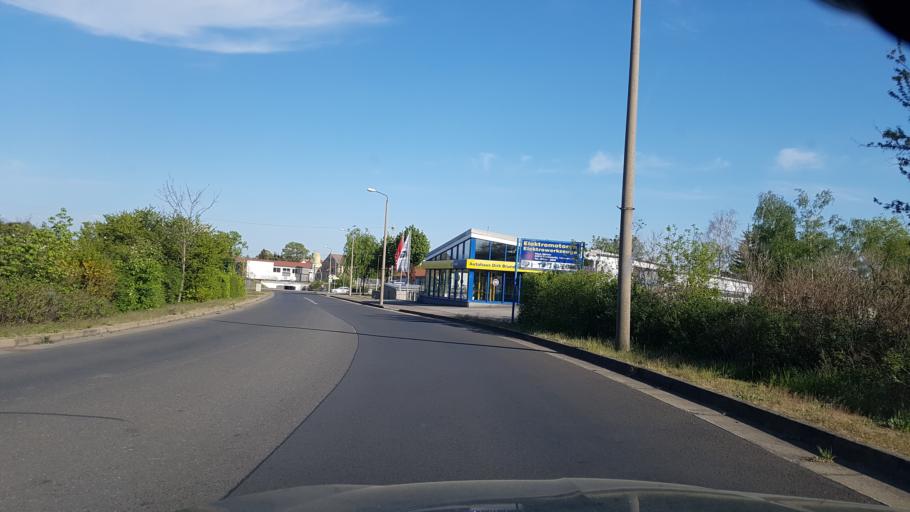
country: DE
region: Brandenburg
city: Elsterwerda
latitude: 51.4629
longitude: 13.5146
